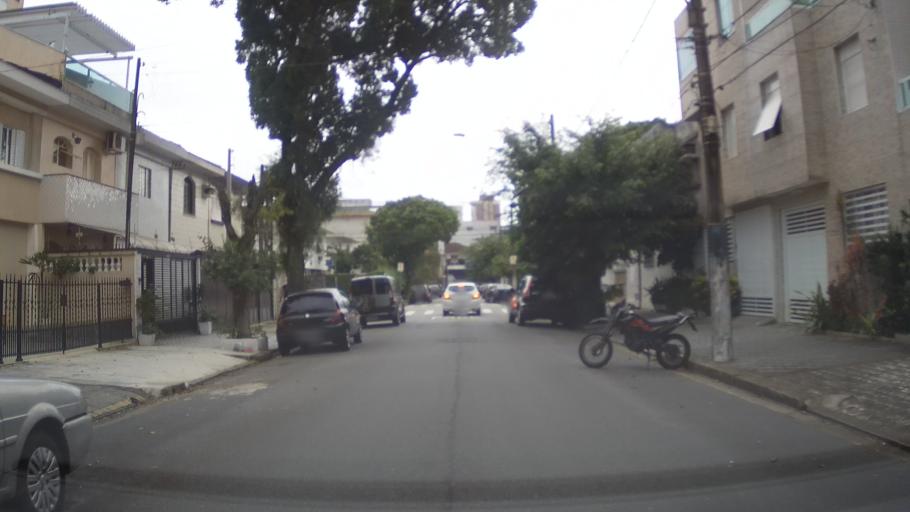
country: BR
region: Sao Paulo
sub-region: Santos
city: Santos
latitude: -23.9616
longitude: -46.3185
